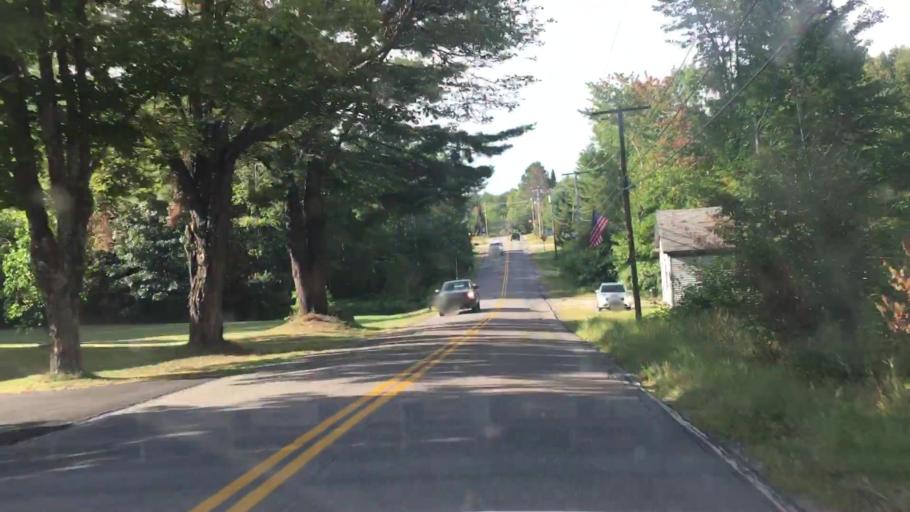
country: US
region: Maine
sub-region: Penobscot County
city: Enfield
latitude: 45.2443
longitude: -68.5651
